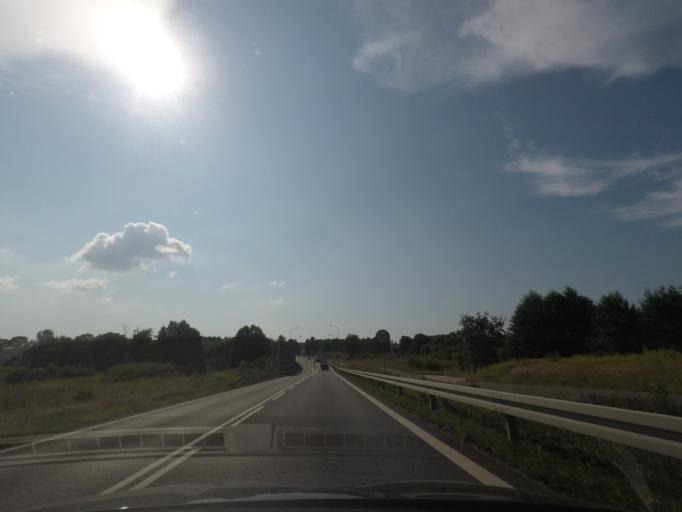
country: PL
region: Silesian Voivodeship
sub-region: Powiat pszczynski
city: Czarkow
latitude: 50.0018
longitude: 18.9132
